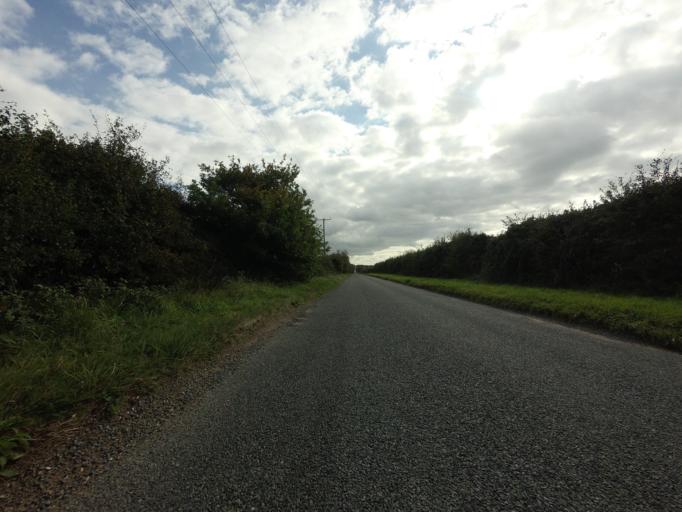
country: GB
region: England
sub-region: Norfolk
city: Heacham
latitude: 52.9124
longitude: 0.5429
